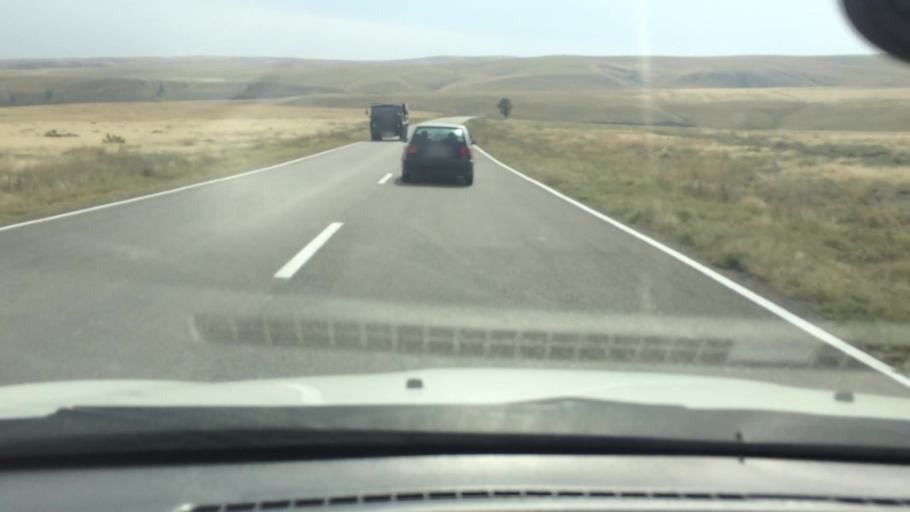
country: GE
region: Kvemo Kartli
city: Rust'avi
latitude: 41.5280
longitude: 44.9385
